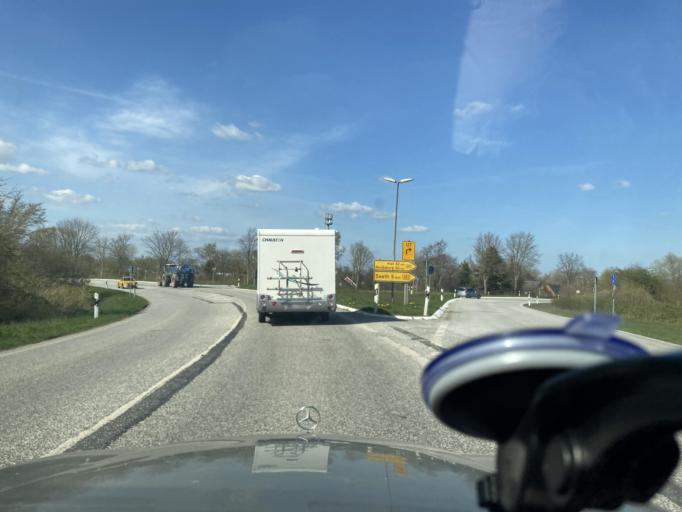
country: DE
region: Schleswig-Holstein
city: Friedrichstadt
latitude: 54.3703
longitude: 9.0969
